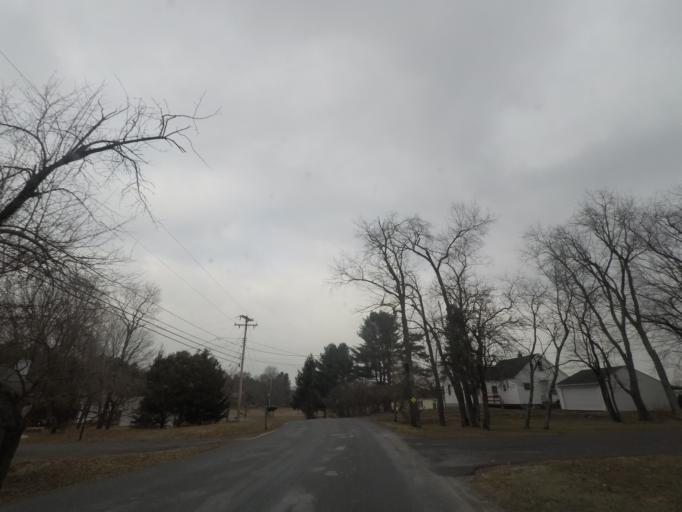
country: US
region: New York
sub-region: Rensselaer County
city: East Greenbush
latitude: 42.5781
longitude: -73.6714
